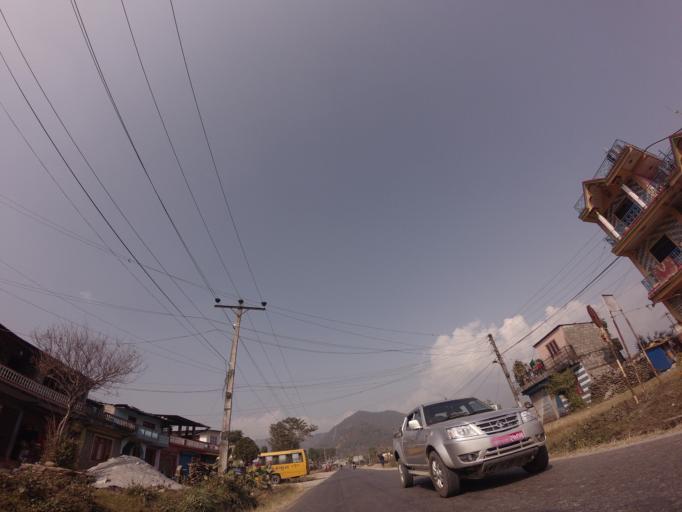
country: NP
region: Western Region
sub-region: Gandaki Zone
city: Pokhara
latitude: 28.2758
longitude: 83.9389
